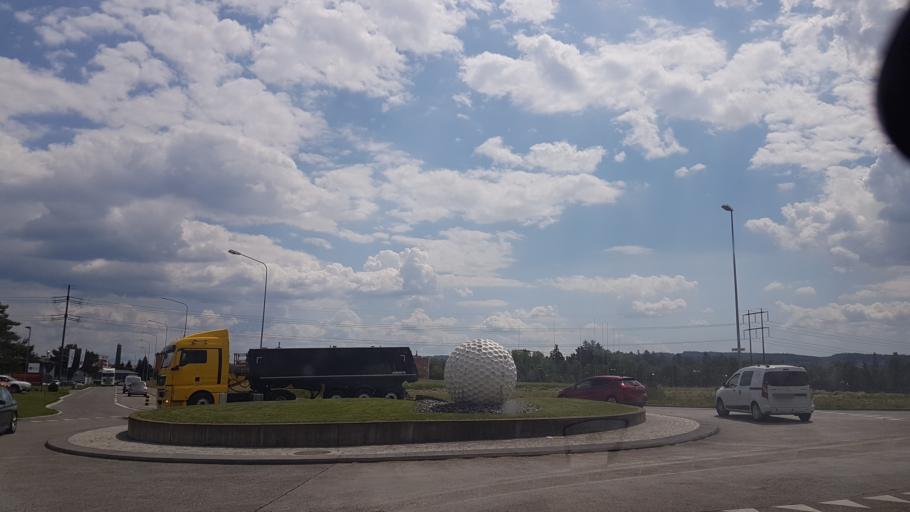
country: CH
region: Zurich
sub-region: Bezirk Uster
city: Greifensee / Muellerwis / Seilerwis
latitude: 47.3783
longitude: 8.6764
